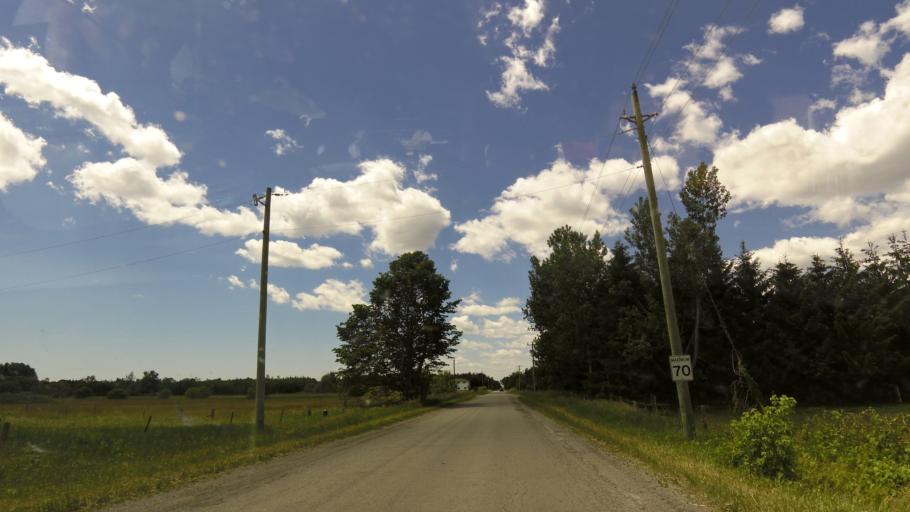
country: CA
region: Ontario
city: Oshawa
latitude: 43.9608
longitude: -78.5689
